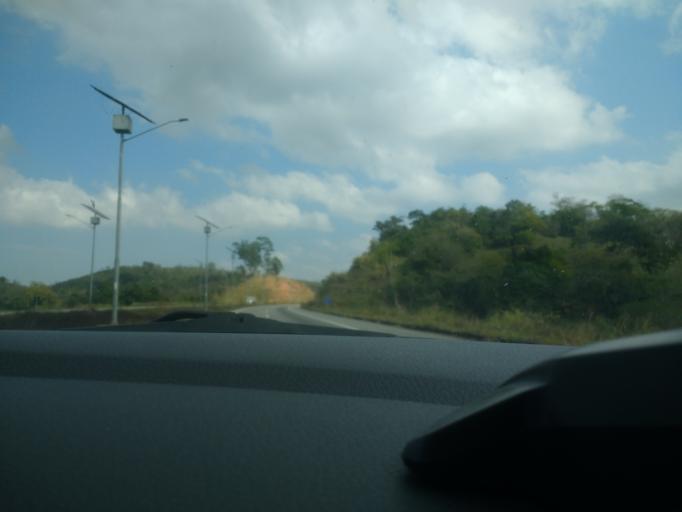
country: BR
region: Rio de Janeiro
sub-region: Queimados
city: Queimados
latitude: -22.6651
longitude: -43.5879
